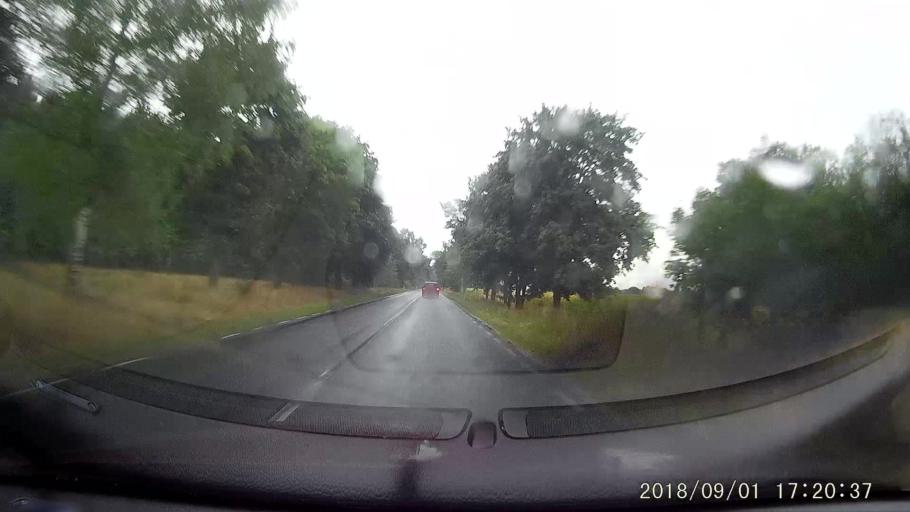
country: PL
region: Lubusz
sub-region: Powiat zielonogorski
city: Nowogrod Bobrzanski
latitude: 51.7225
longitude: 15.2805
